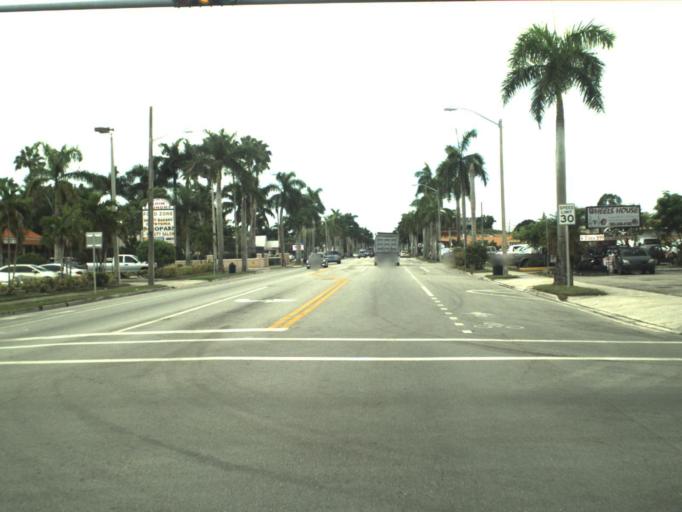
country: US
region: Florida
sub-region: Miami-Dade County
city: Homestead
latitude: 25.4845
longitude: -80.4775
